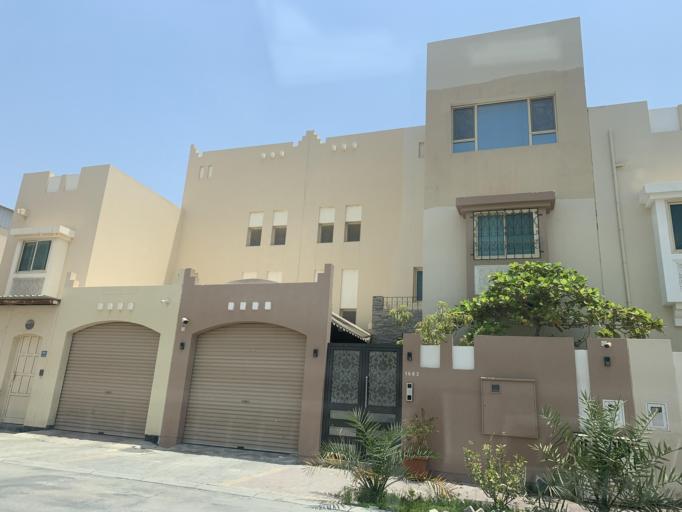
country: BH
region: Manama
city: Jidd Hafs
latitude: 26.2105
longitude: 50.4714
